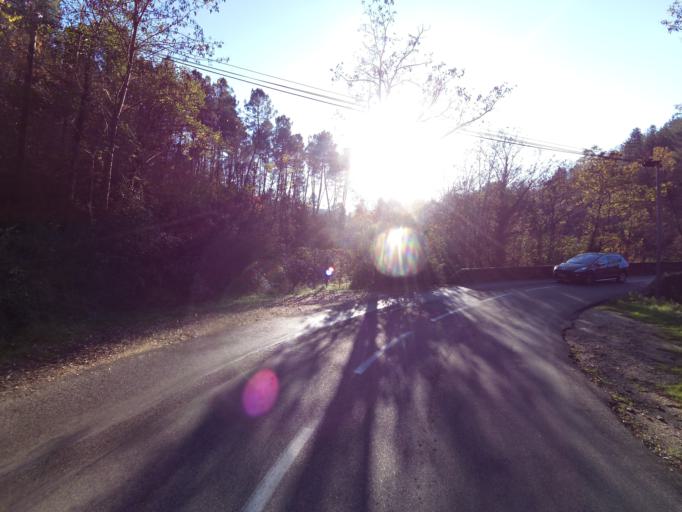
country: FR
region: Rhone-Alpes
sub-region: Departement de l'Ardeche
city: Joyeuse
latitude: 44.4957
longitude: 4.2191
